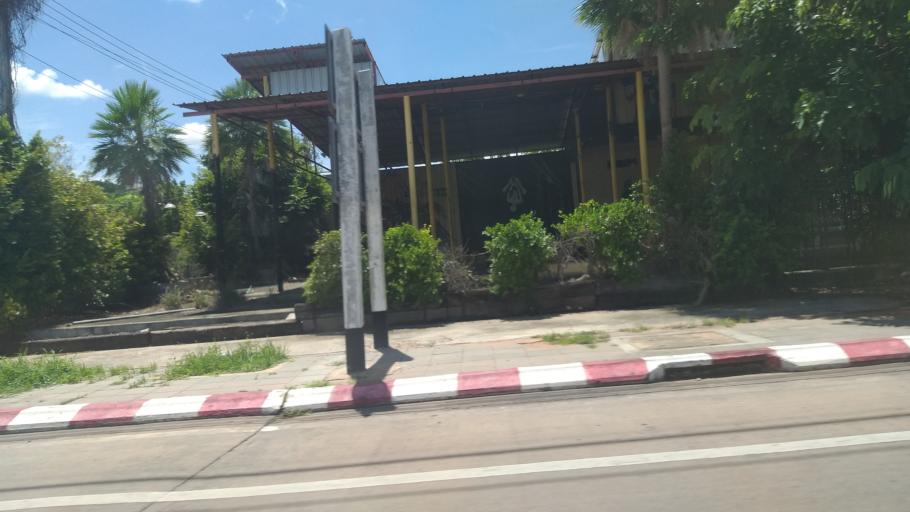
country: TH
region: Khon Kaen
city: Khon Kaen
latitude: 16.4373
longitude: 102.8193
